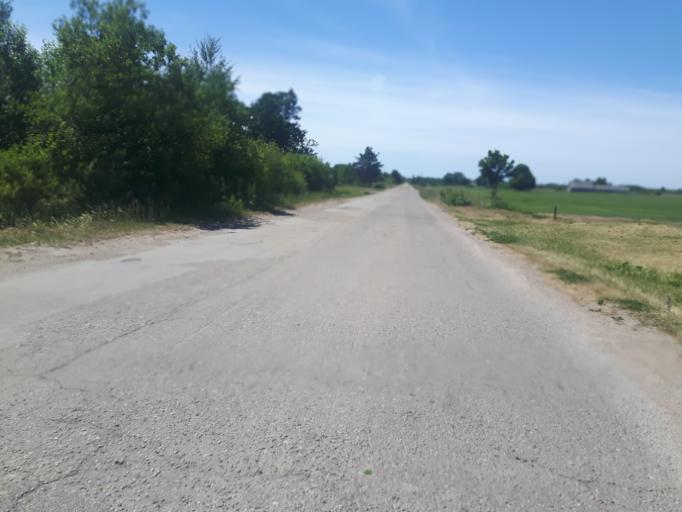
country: LV
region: Grobina
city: Grobina
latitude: 56.5301
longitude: 21.1524
